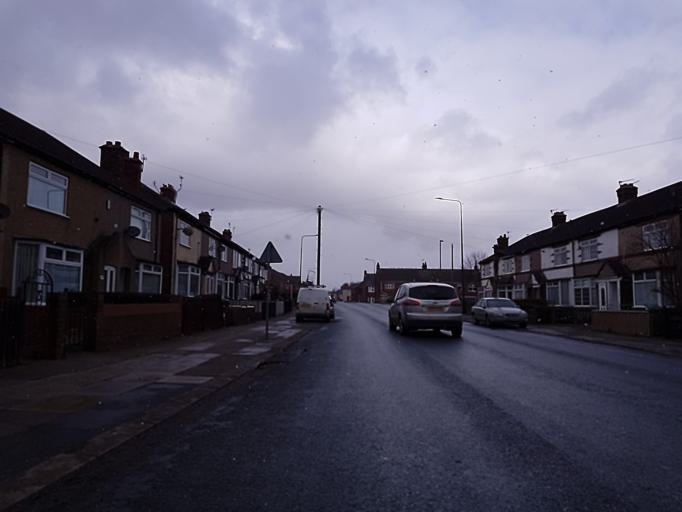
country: GB
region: England
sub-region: North East Lincolnshire
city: Grimbsy
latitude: 53.5705
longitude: -0.0986
